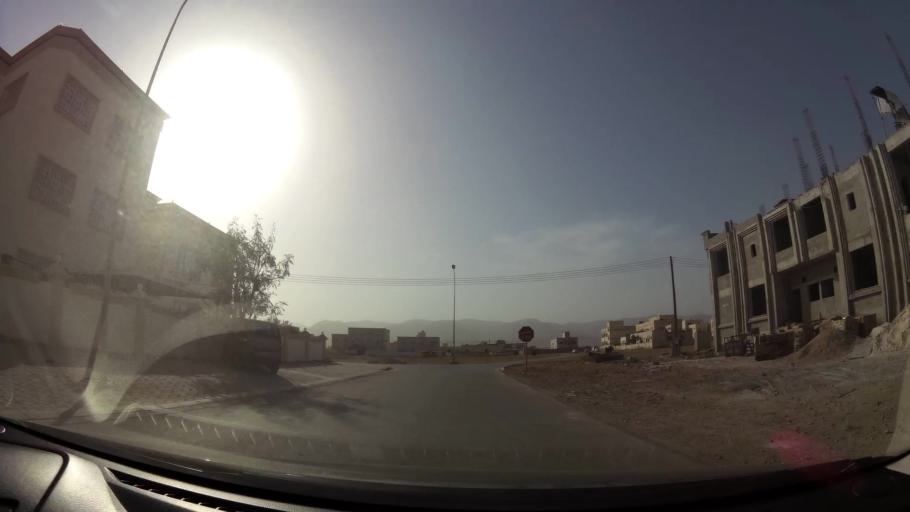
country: OM
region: Zufar
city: Salalah
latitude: 17.0208
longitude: 54.0197
